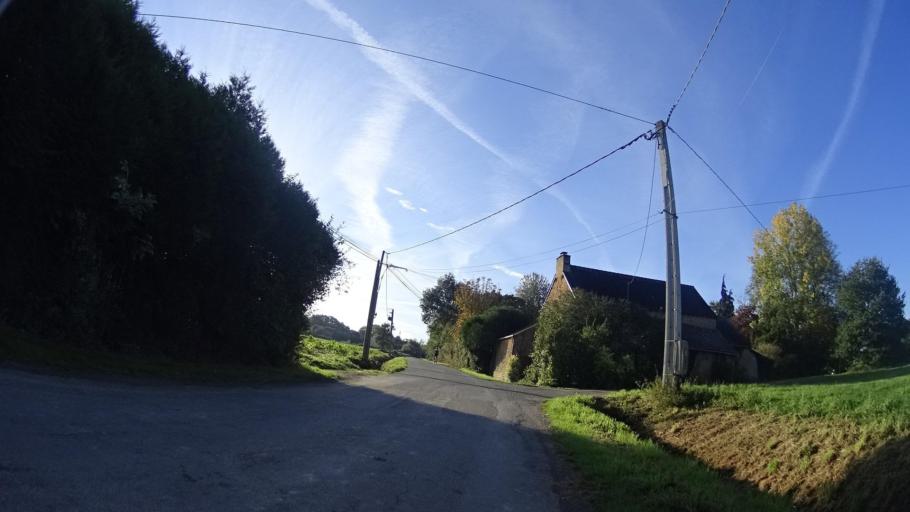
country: FR
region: Brittany
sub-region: Departement des Cotes-d'Armor
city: Evran
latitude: 48.3412
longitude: -1.9387
